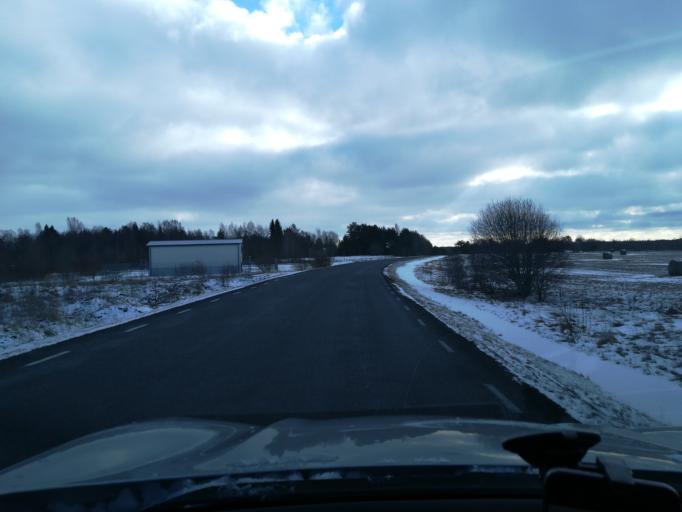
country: EE
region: Harju
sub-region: Harku vald
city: Tabasalu
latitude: 59.4222
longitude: 24.4212
